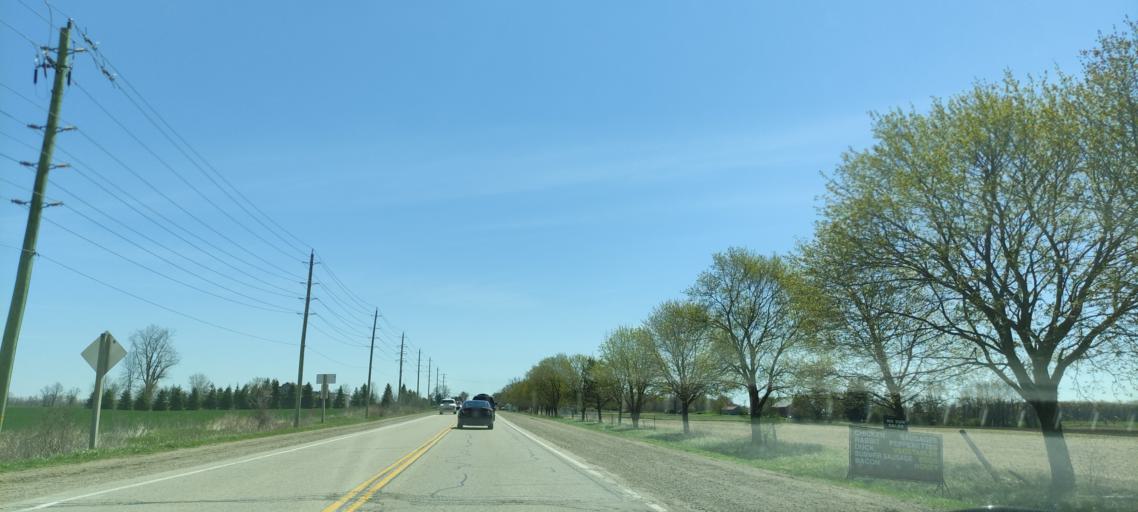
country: CA
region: Ontario
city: Waterloo
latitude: 43.5866
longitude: -80.4641
